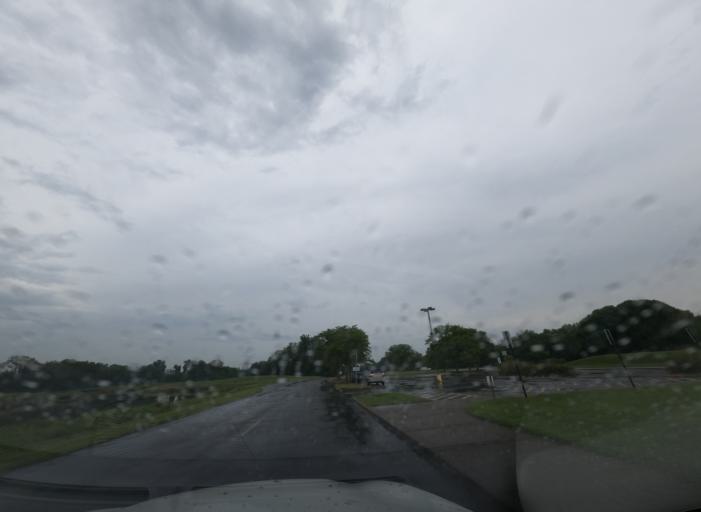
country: US
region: Illinois
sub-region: Saint Clair County
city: Fairmont City
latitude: 38.6543
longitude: -90.0586
